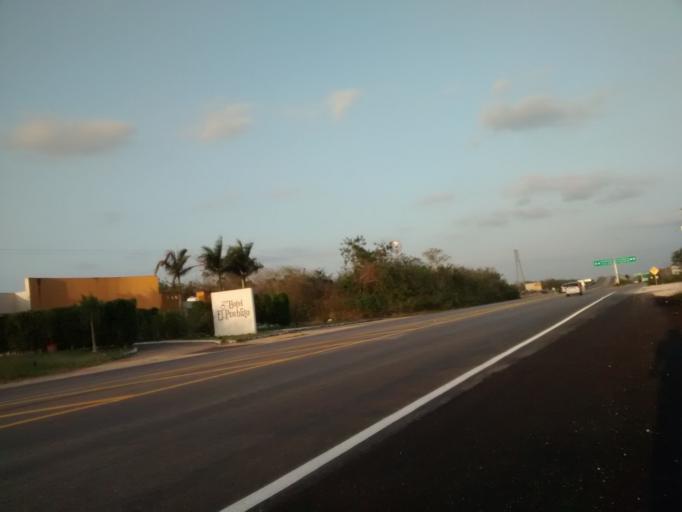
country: MX
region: Yucatan
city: Valladolid
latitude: 20.7251
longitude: -88.2082
